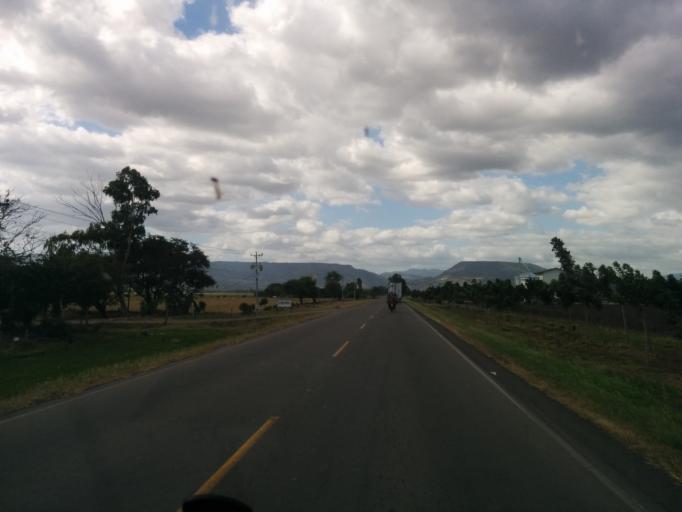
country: NI
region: Matagalpa
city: Ciudad Dario
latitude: 12.8841
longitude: -86.1466
